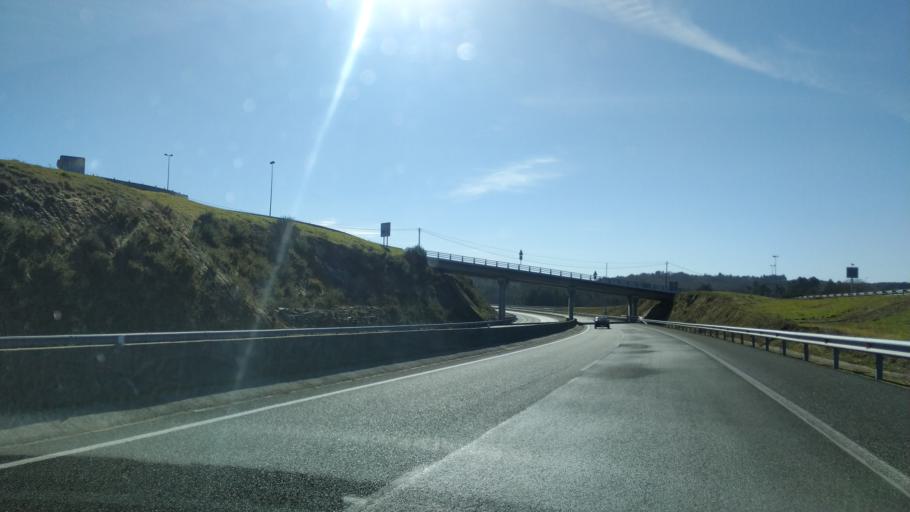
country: ES
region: Galicia
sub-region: Provincia de Pontevedra
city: Lalin
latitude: 42.6396
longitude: -8.1324
